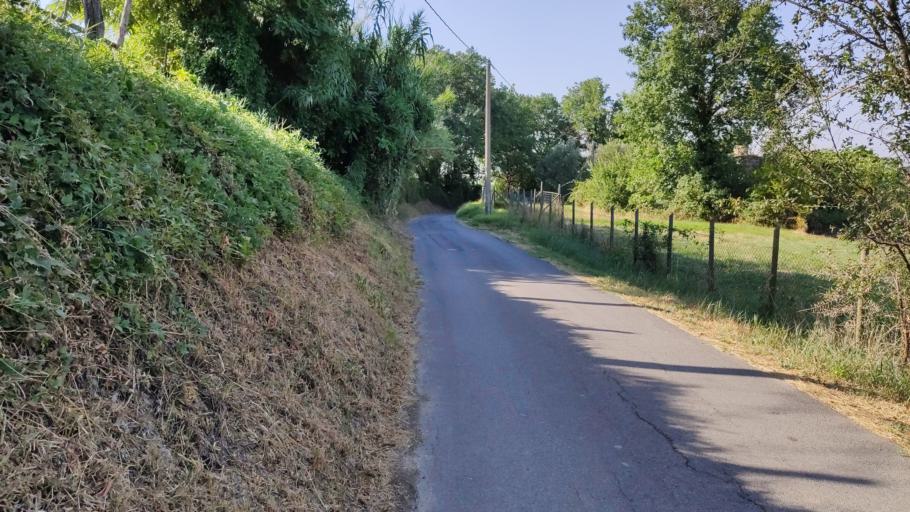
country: IT
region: Umbria
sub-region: Provincia di Terni
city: Amelia
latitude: 42.5381
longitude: 12.4116
